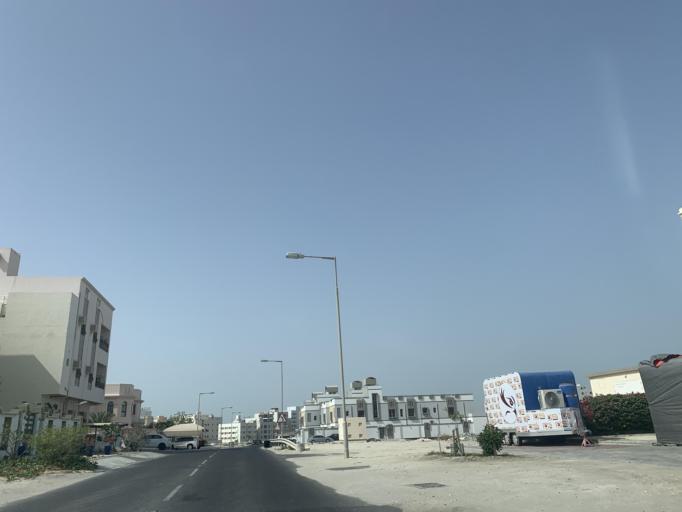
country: BH
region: Northern
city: Ar Rifa'
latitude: 26.1461
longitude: 50.5694
